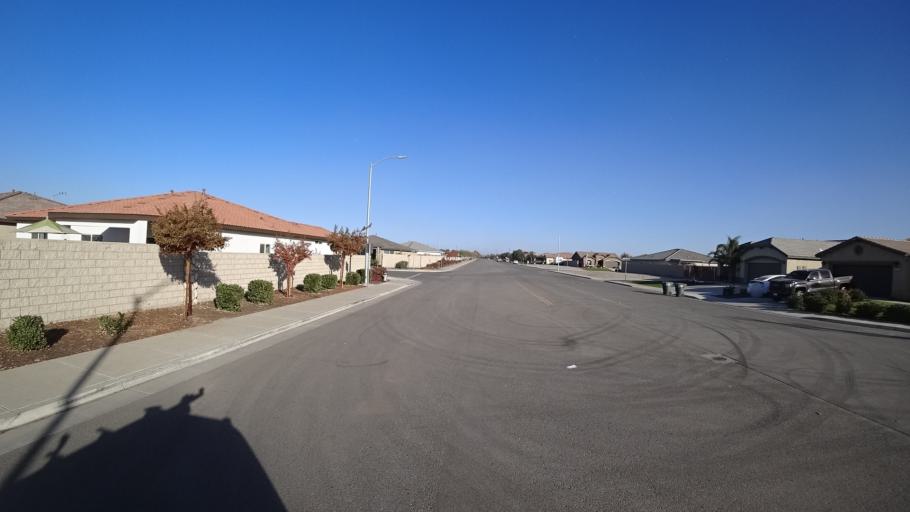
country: US
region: California
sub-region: Kern County
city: Greenfield
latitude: 35.2706
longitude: -119.0303
